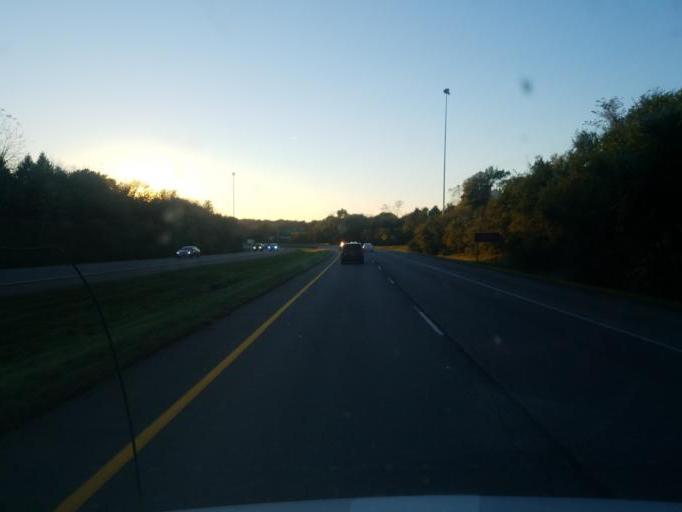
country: US
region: Ohio
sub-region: Stark County
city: Canton
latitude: 40.8306
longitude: -81.3880
